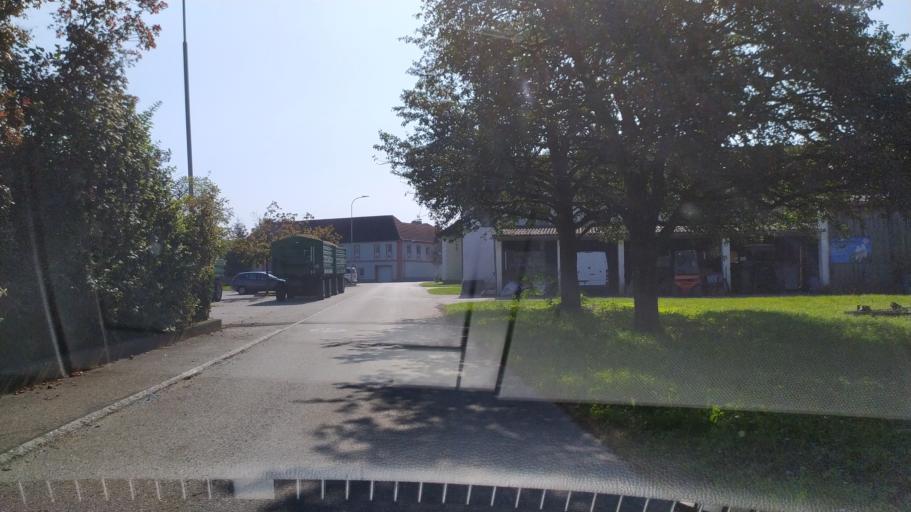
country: AT
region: Lower Austria
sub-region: Politischer Bezirk Amstetten
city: Strengberg
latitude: 48.1864
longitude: 14.7085
